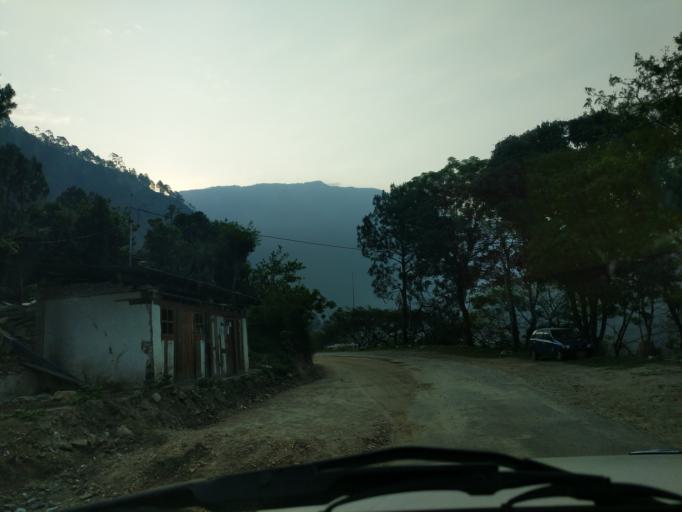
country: BT
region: Mongar
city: Mongar
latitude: 27.2612
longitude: 91.1763
